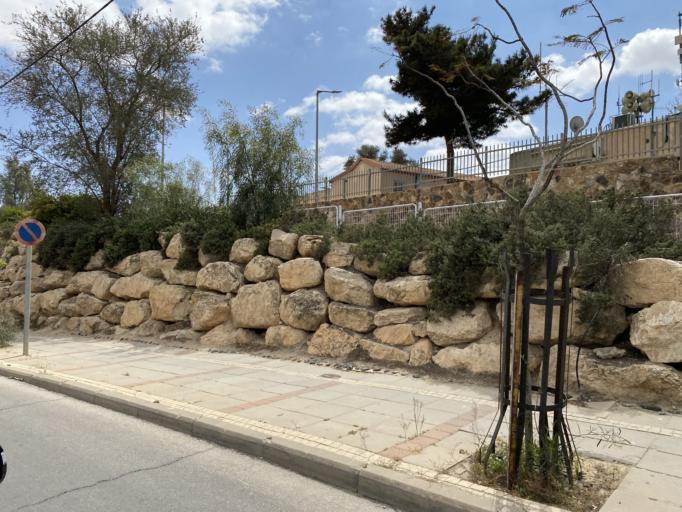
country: IL
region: Southern District
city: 'Arad
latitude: 31.2562
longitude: 35.2135
